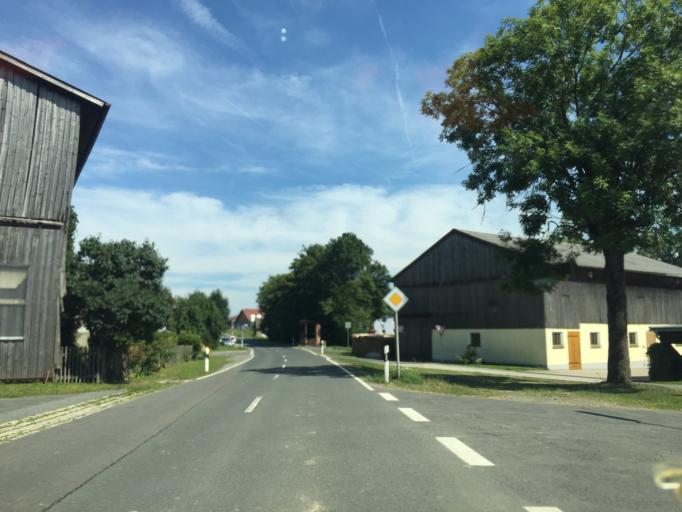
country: DE
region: Bavaria
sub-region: Upper Palatinate
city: Kirchendemenreuth
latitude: 49.7911
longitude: 12.1249
